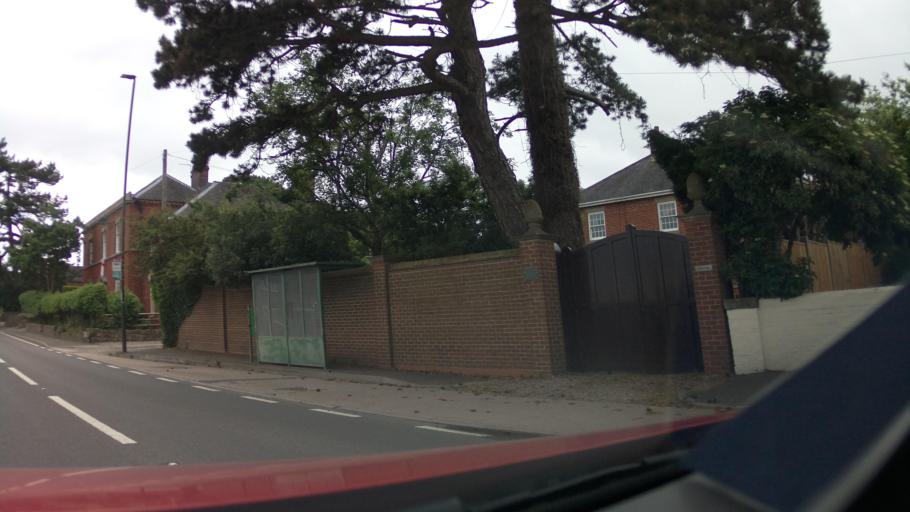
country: GB
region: England
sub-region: Derbyshire
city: Yeldersley
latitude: 52.9672
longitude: -1.6168
